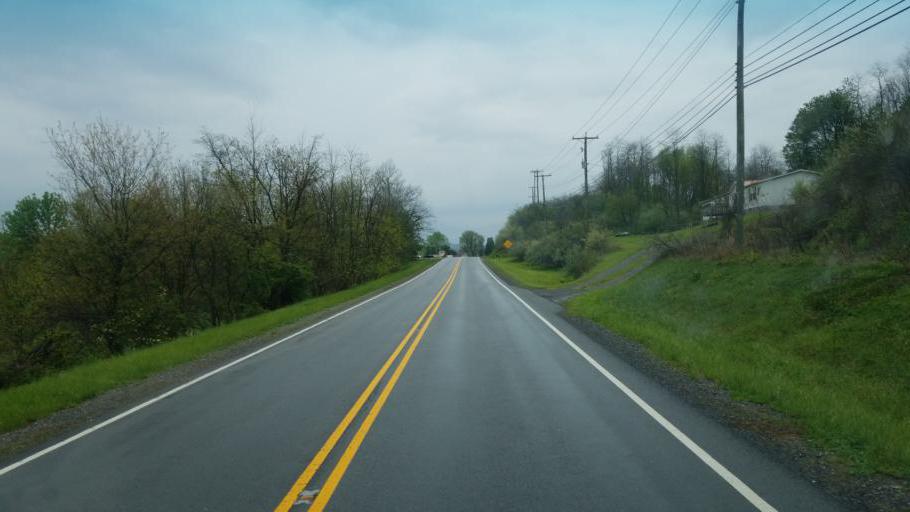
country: US
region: Virginia
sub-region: Smyth County
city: Atkins
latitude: 36.8817
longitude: -81.3804
